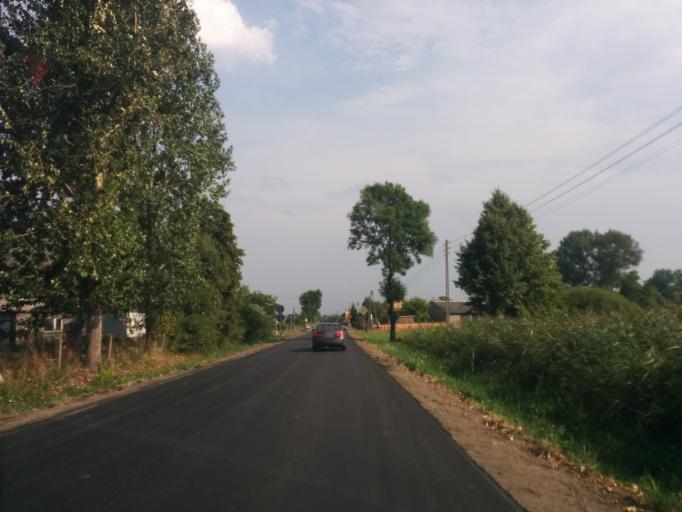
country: PL
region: Silesian Voivodeship
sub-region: Powiat myszkowski
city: Zarki
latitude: 50.6040
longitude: 19.4152
